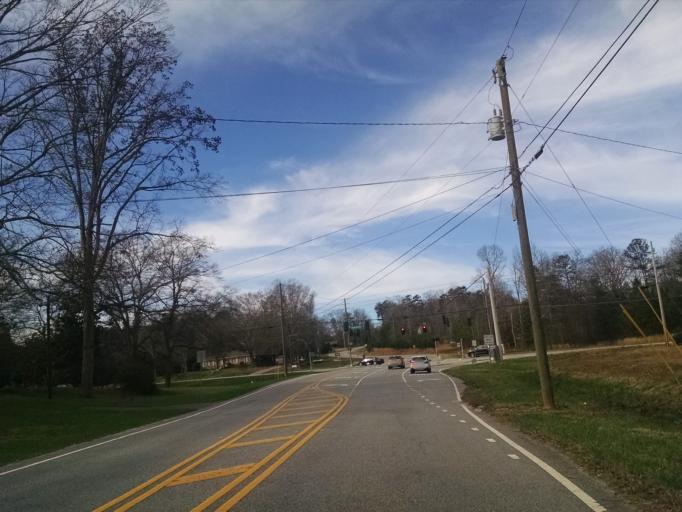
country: US
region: Georgia
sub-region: Gwinnett County
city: Sugar Hill
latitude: 34.0812
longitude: -84.0369
